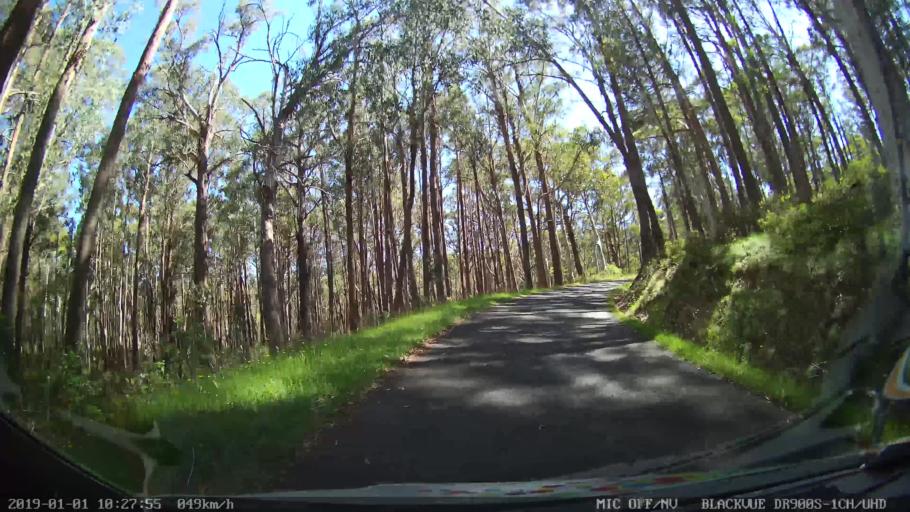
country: AU
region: New South Wales
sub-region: Snowy River
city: Jindabyne
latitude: -36.0630
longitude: 148.2366
